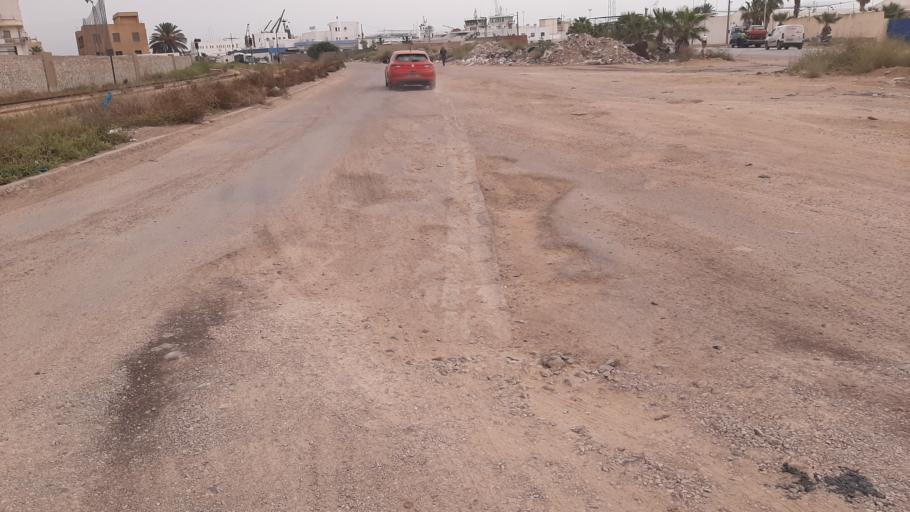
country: TN
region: Safaqis
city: Sfax
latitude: 34.7262
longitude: 10.7608
